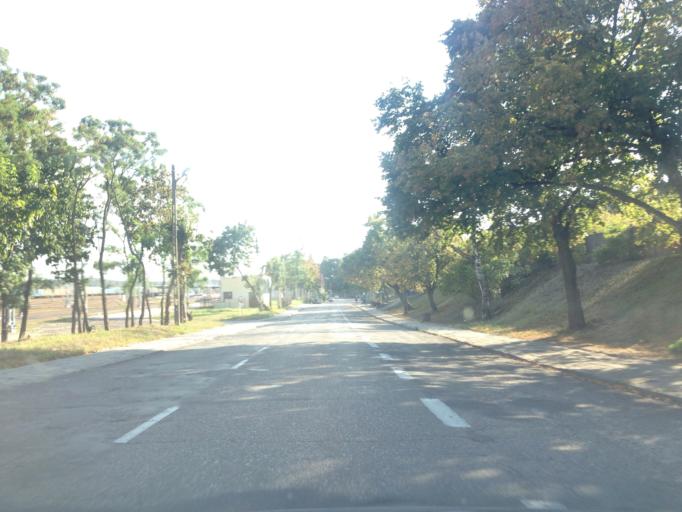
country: PL
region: Warmian-Masurian Voivodeship
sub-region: Powiat ilawski
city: Ilawa
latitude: 53.5850
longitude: 19.5746
